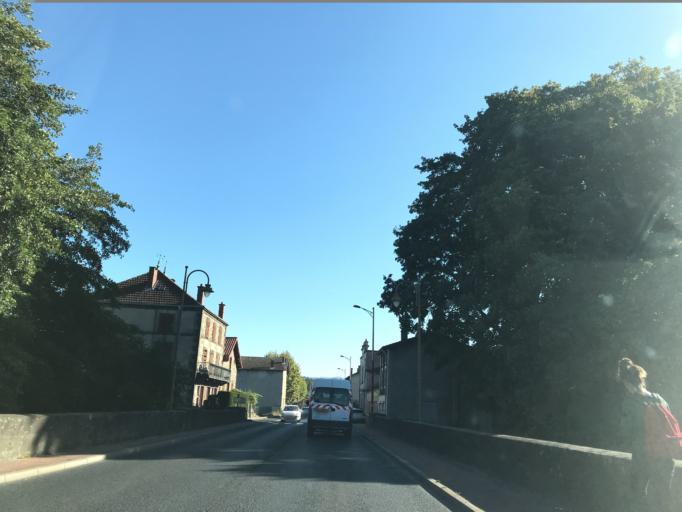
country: FR
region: Auvergne
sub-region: Departement du Puy-de-Dome
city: Courpiere
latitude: 45.7556
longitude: 3.5426
